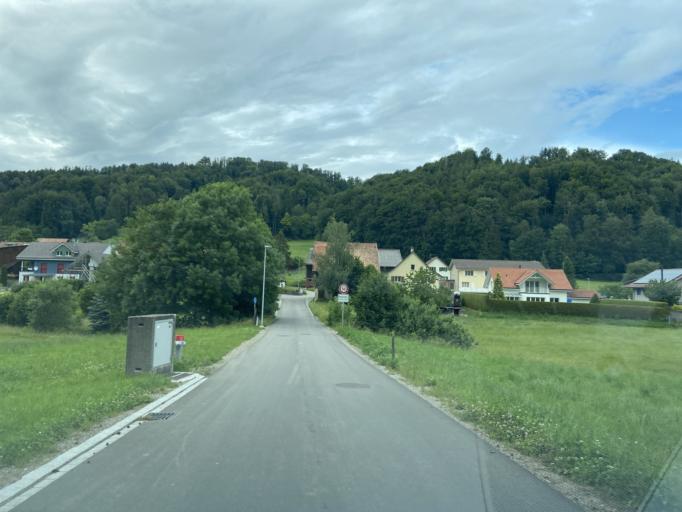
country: CH
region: Thurgau
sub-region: Muenchwilen District
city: Aadorf
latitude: 47.4553
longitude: 8.9095
